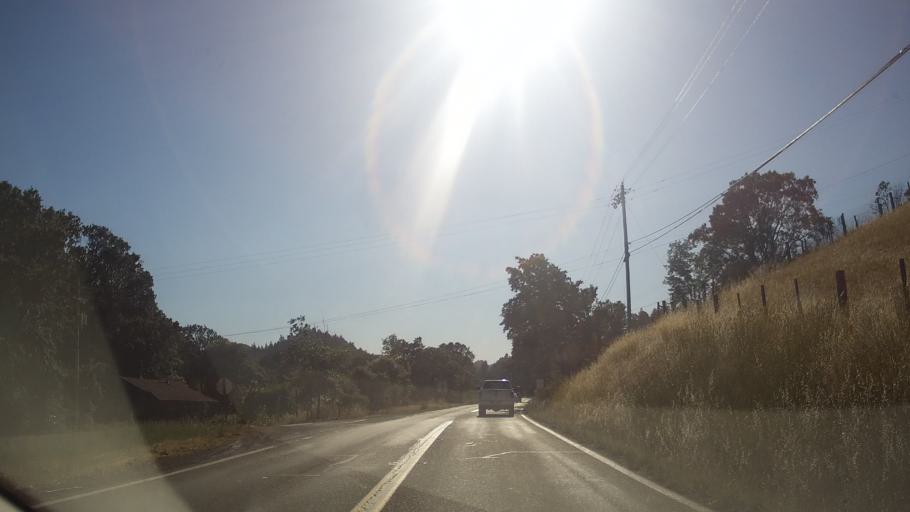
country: US
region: California
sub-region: Mendocino County
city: Willits
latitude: 39.4055
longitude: -123.3637
